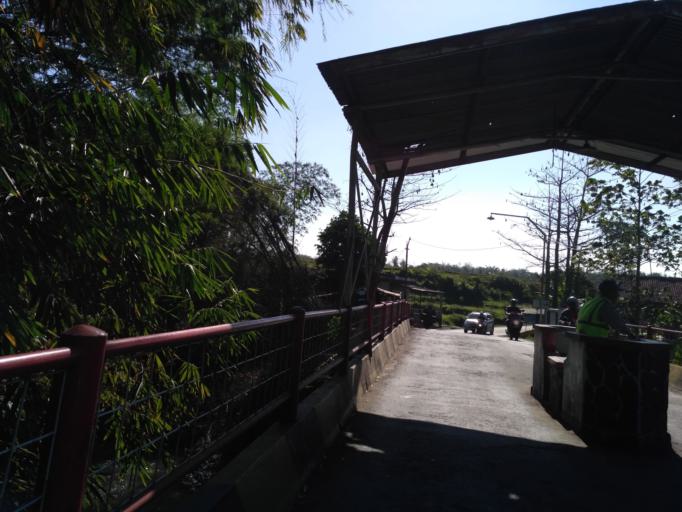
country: ID
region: East Java
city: Singosari
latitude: -7.9302
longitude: 112.6626
